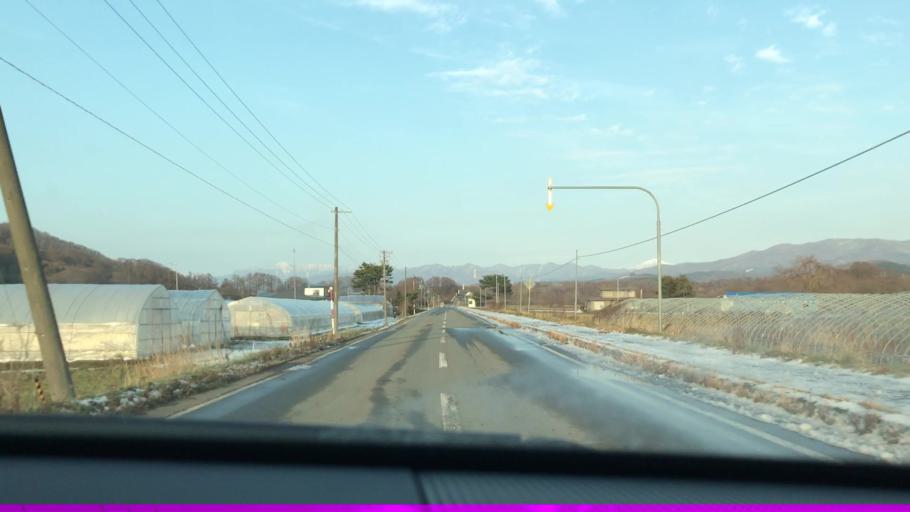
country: JP
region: Hokkaido
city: Shizunai-furukawacho
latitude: 42.4189
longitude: 142.3981
